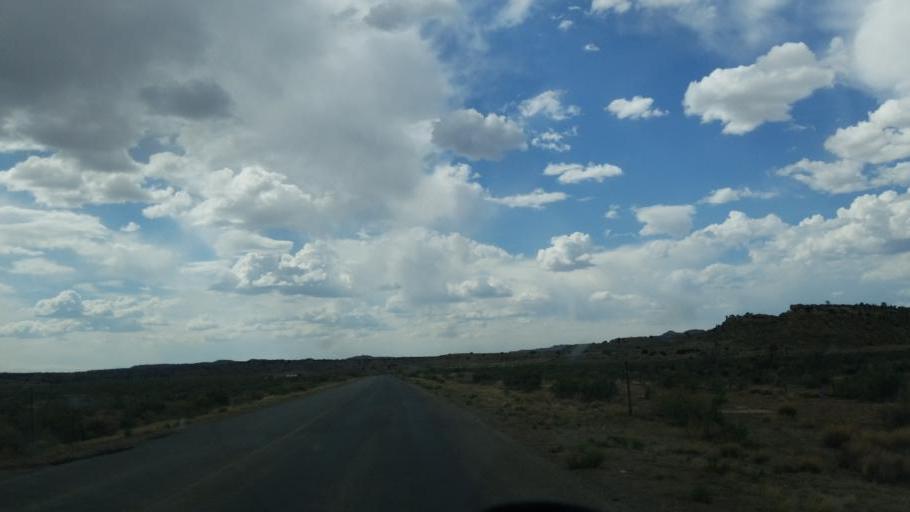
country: US
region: New Mexico
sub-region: McKinley County
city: Gallup
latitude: 35.4934
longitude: -108.9093
